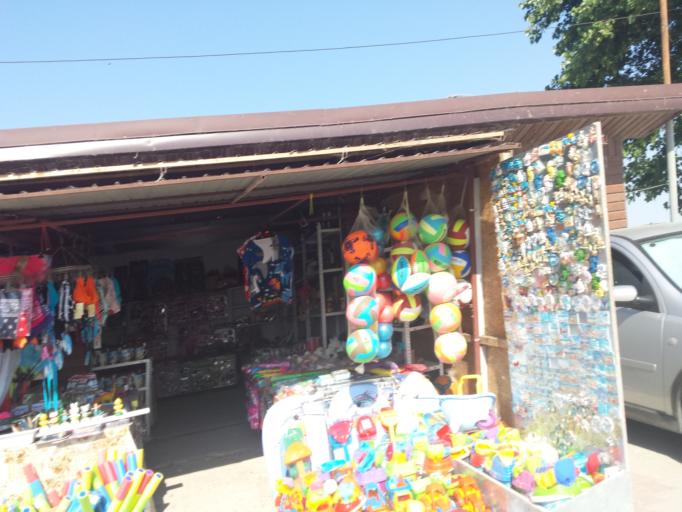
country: RO
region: Constanta
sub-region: Comuna Douazeci si Trei August
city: Douazeci si Trei August
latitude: 43.8606
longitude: 28.6062
